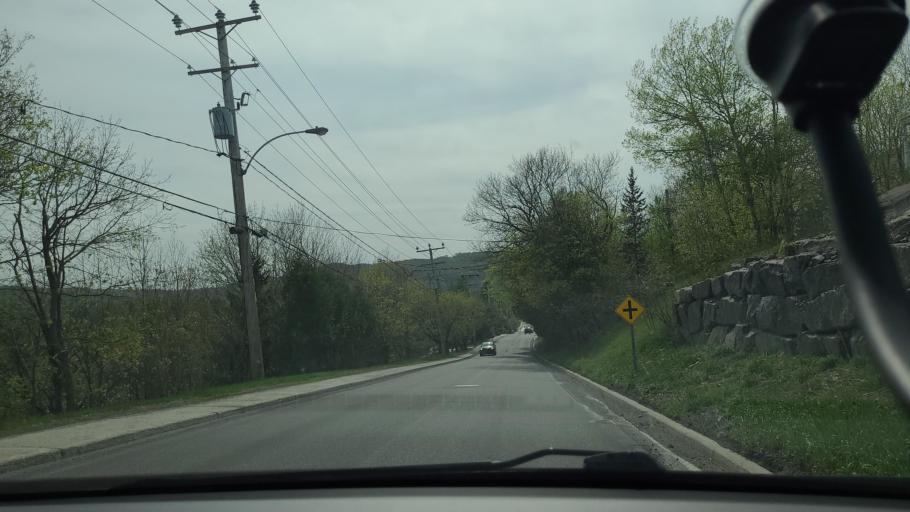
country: CA
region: Quebec
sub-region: Laurentides
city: Prevost
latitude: 45.8748
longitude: -74.0712
